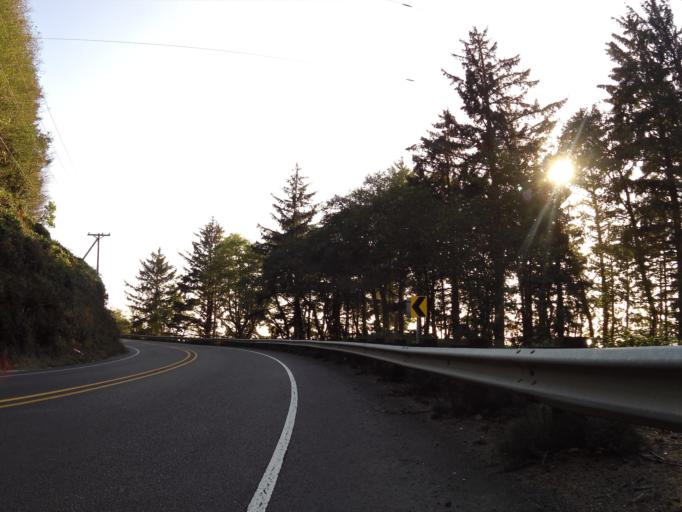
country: US
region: Oregon
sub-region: Tillamook County
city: Rockaway Beach
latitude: 45.6887
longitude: -123.9240
